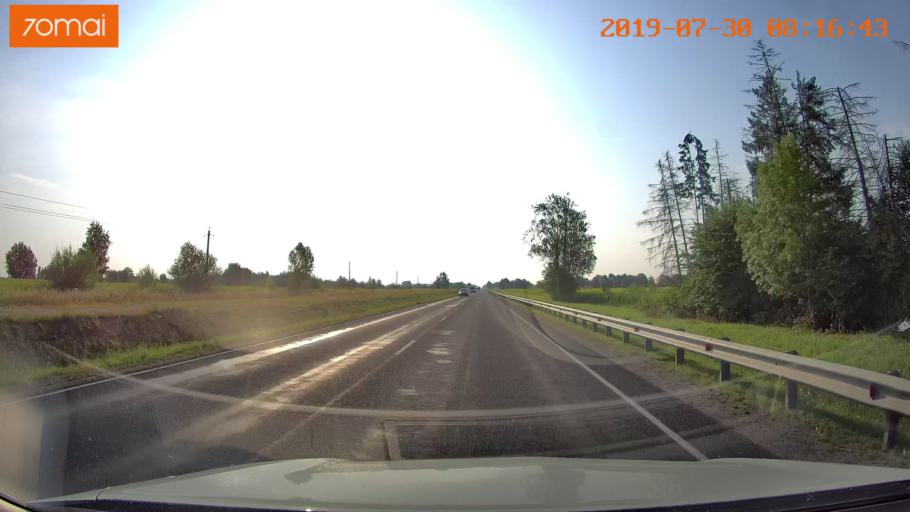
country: RU
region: Kaliningrad
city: Zheleznodorozhnyy
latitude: 54.6392
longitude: 21.4183
